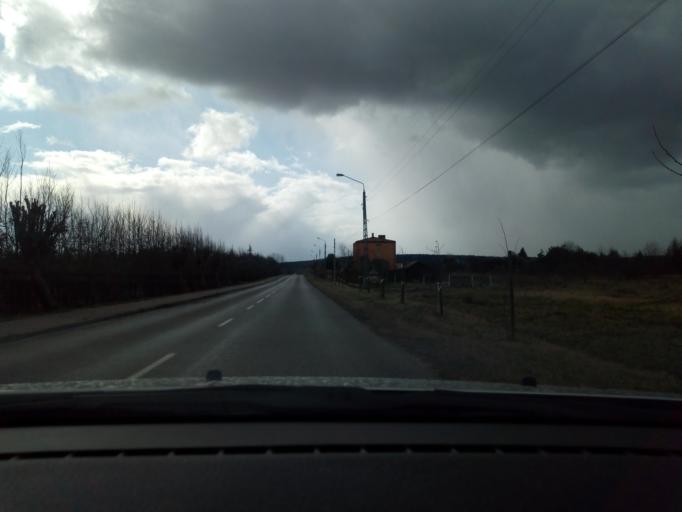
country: PL
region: Swietokrzyskie
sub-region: Powiat skarzyski
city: Skarzysko Koscielne
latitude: 51.1493
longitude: 20.8914
